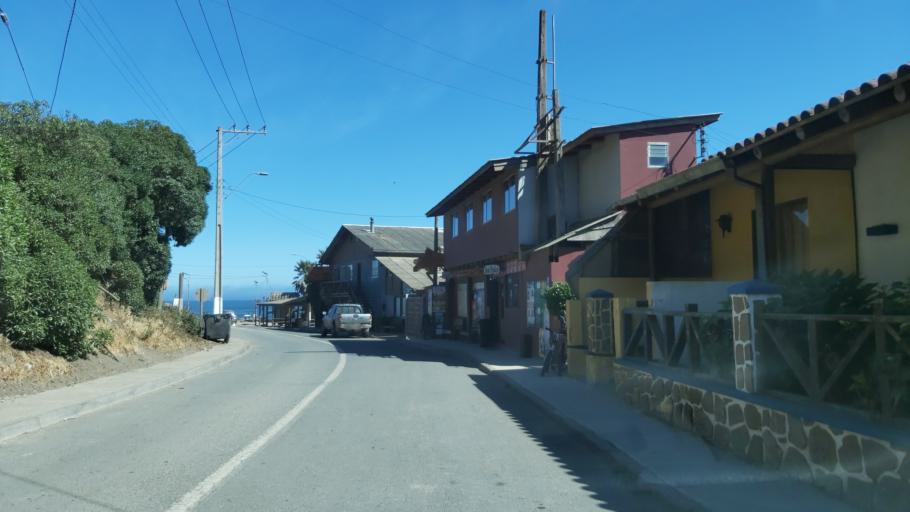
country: CL
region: Maule
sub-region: Provincia de Talca
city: Constitucion
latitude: -34.7543
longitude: -72.0850
